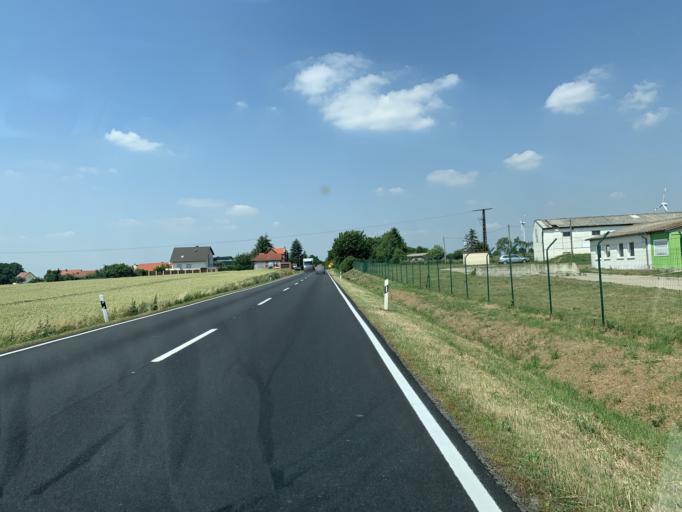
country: DE
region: Saxony-Anhalt
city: Erxleben
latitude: 52.1775
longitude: 11.2676
